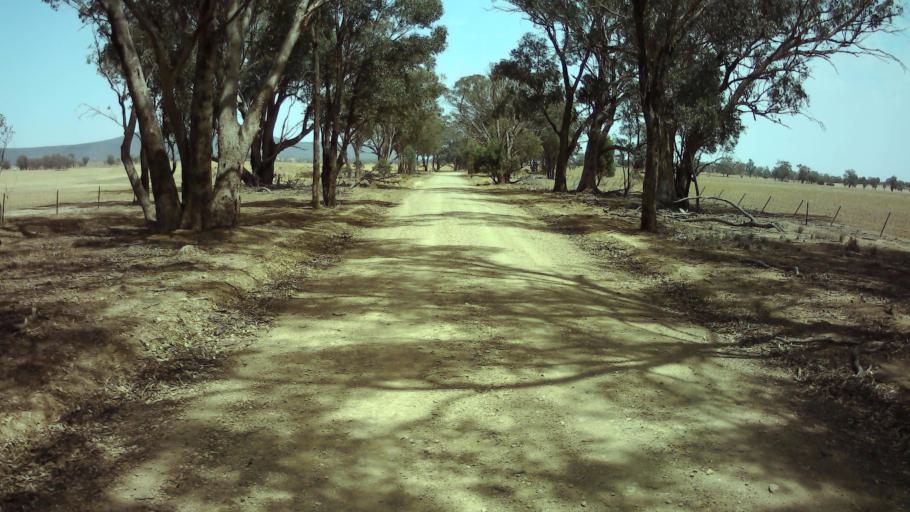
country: AU
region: New South Wales
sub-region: Weddin
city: Grenfell
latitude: -33.8843
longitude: 148.0782
